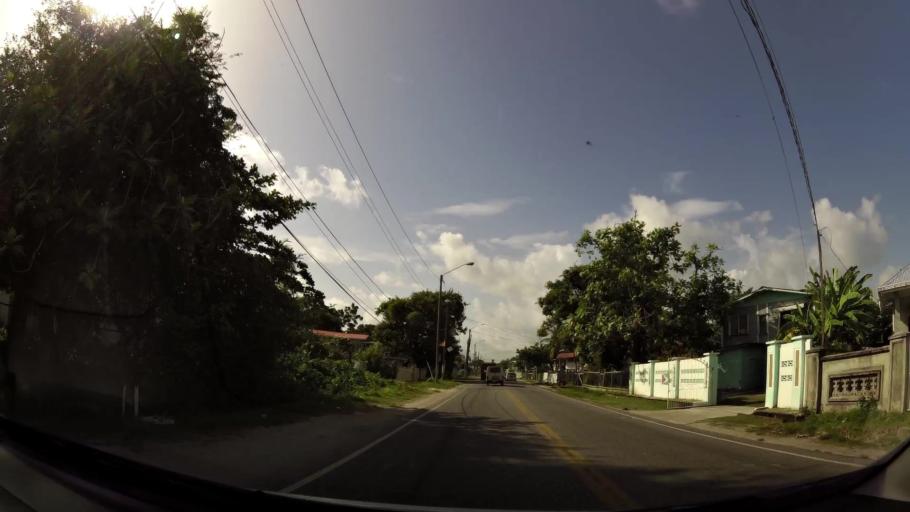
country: GY
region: Demerara-Mahaica
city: Mahaica Village
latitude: 6.7578
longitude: -57.9784
